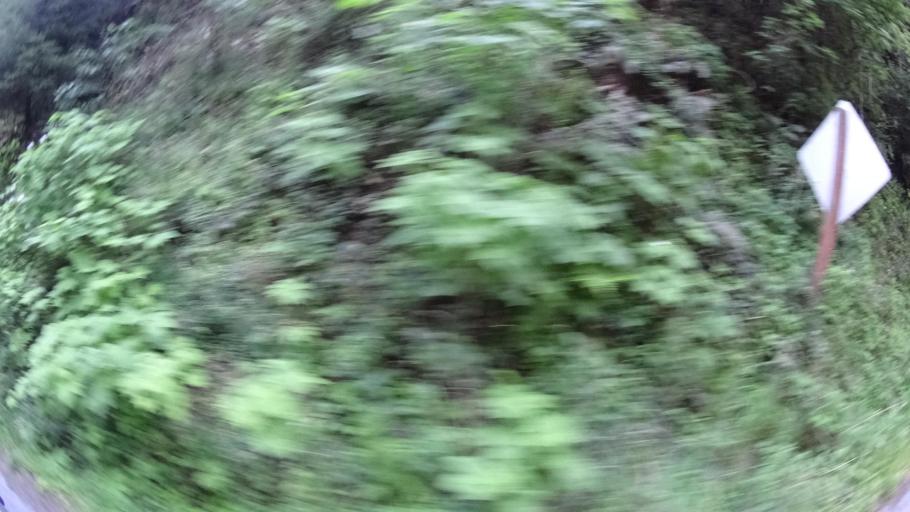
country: US
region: California
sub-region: Humboldt County
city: Rio Dell
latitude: 40.4528
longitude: -123.9804
